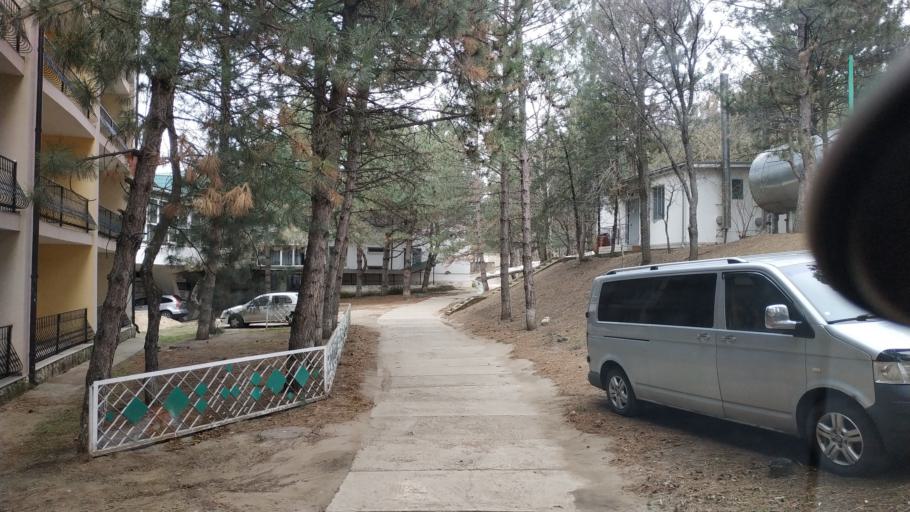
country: MD
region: Telenesti
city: Cocieri
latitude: 47.3317
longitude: 29.0839
